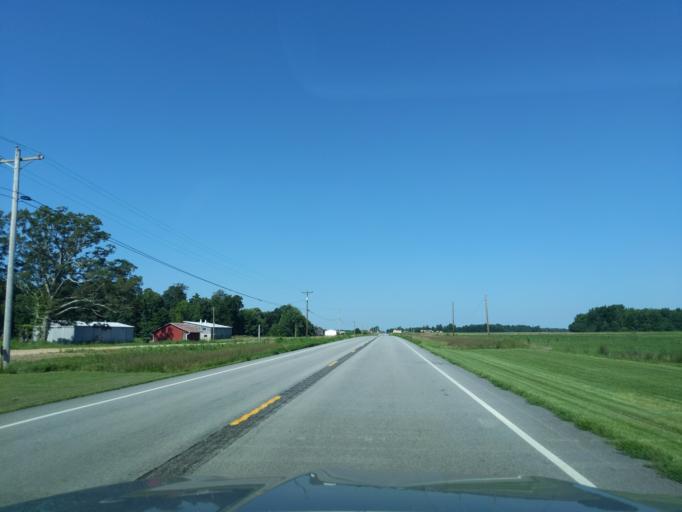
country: US
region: Indiana
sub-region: Ripley County
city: Versailles
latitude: 39.0750
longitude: -85.2802
